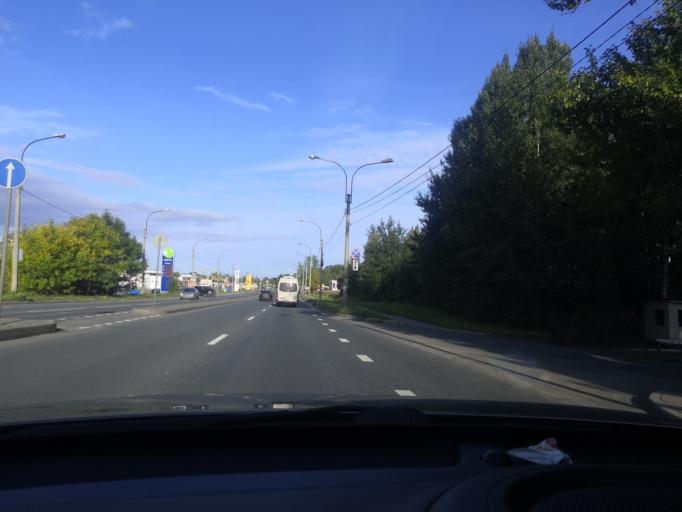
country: RU
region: St.-Petersburg
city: Pargolovo
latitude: 60.0762
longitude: 30.2742
